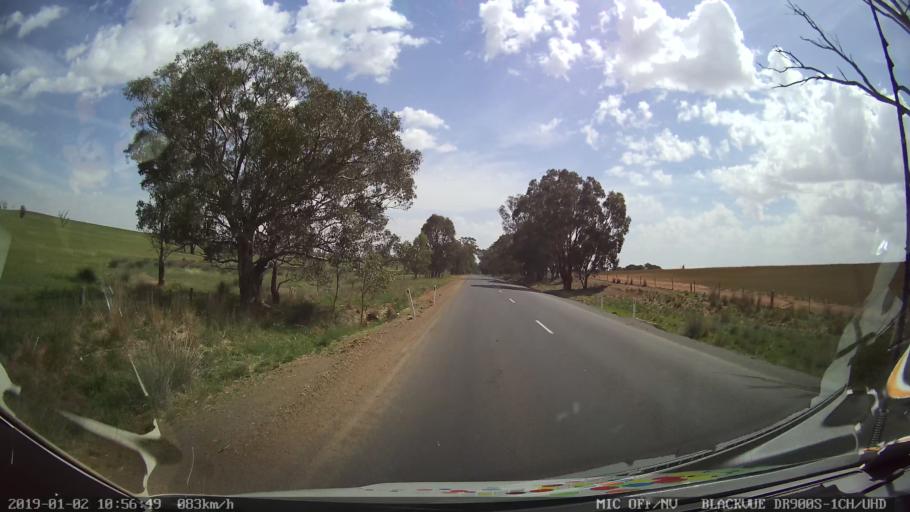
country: AU
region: New South Wales
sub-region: Cootamundra
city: Cootamundra
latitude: -34.6427
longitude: 148.2791
